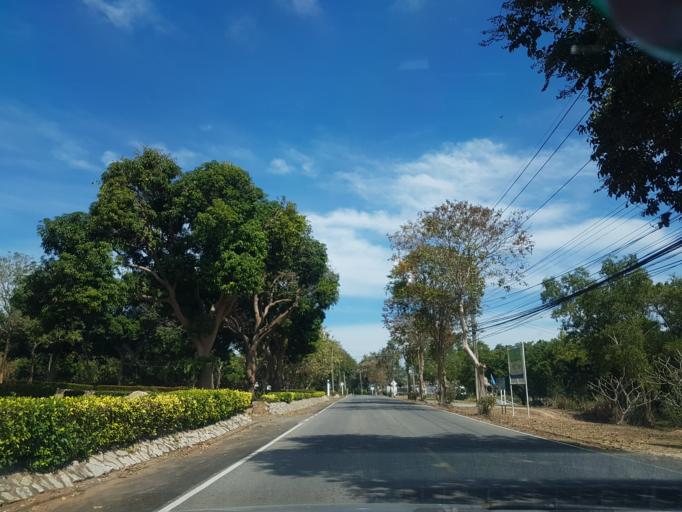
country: TH
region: Chon Buri
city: Sattahip
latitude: 12.6347
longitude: 100.9379
